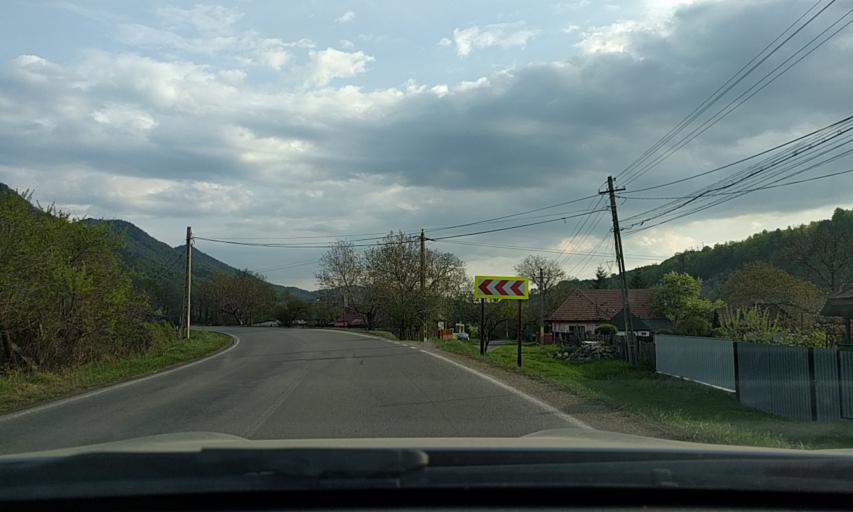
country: RO
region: Bacau
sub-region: Oras Slanic-Moldova
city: Slanic-Moldova
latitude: 46.1484
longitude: 26.4595
